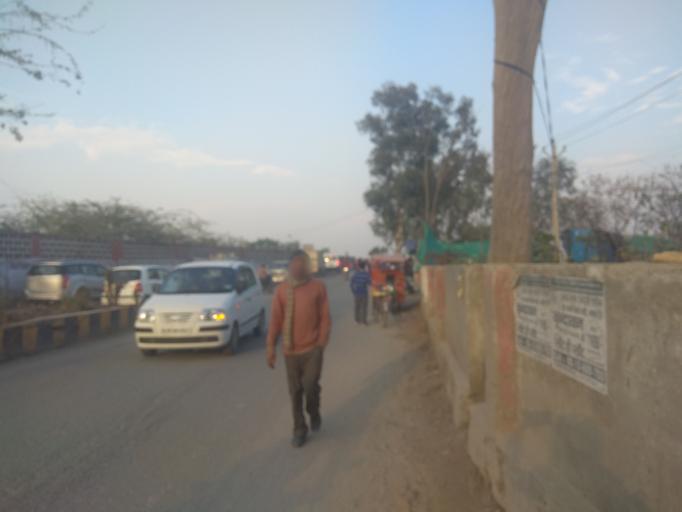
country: IN
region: NCT
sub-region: West Delhi
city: Nangloi Jat
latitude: 28.6391
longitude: 77.0607
